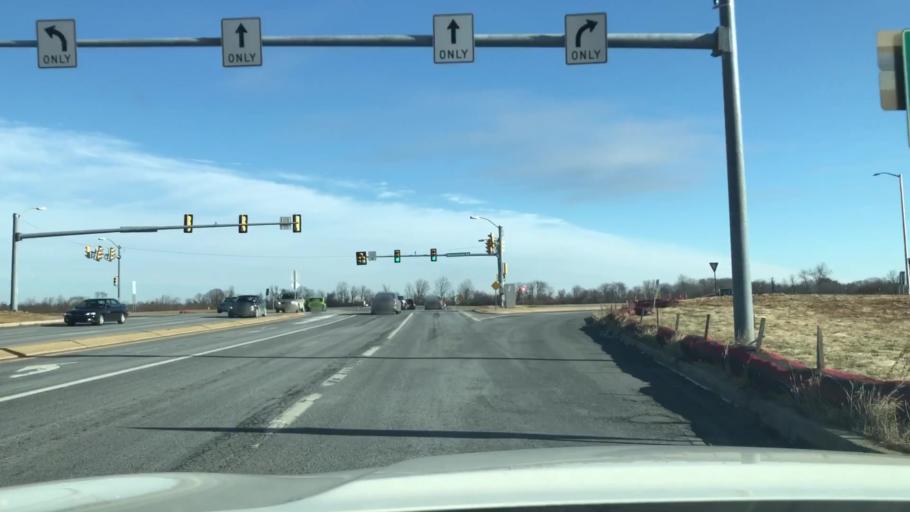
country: US
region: Pennsylvania
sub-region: Lehigh County
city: Catasauqua
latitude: 40.6668
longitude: -75.4227
